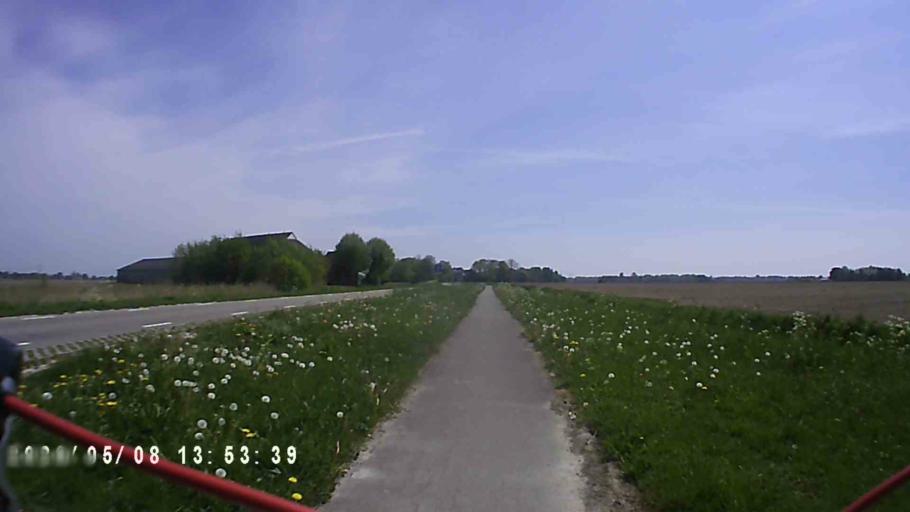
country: NL
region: Groningen
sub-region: Gemeente Appingedam
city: Appingedam
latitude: 53.3385
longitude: 6.7841
